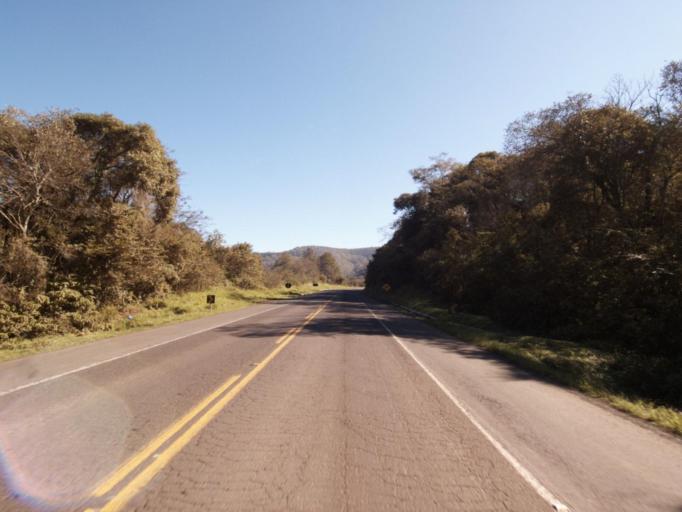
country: BR
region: Rio Grande do Sul
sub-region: Frederico Westphalen
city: Frederico Westphalen
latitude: -27.0342
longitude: -53.2331
